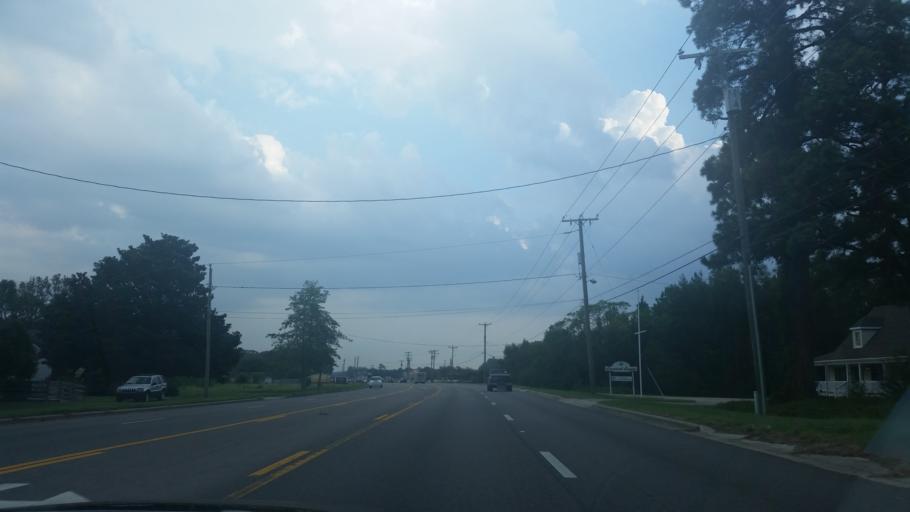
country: US
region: North Carolina
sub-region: Dare County
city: Southern Shores
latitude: 36.2312
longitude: -75.8736
